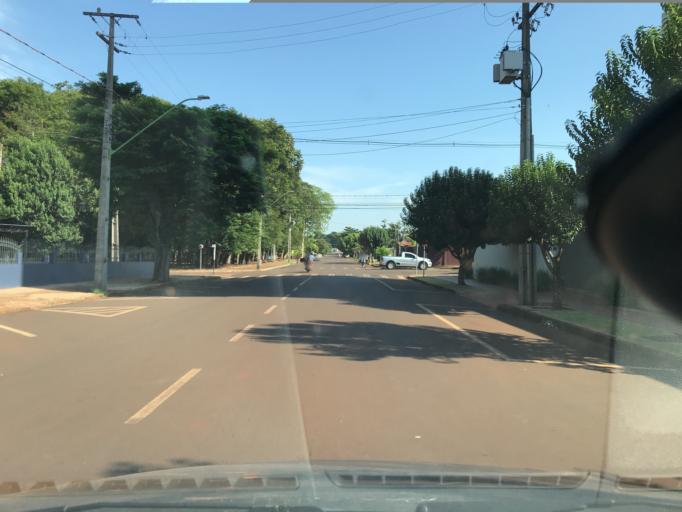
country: BR
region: Parana
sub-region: Palotina
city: Palotina
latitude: -24.2833
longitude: -53.8425
